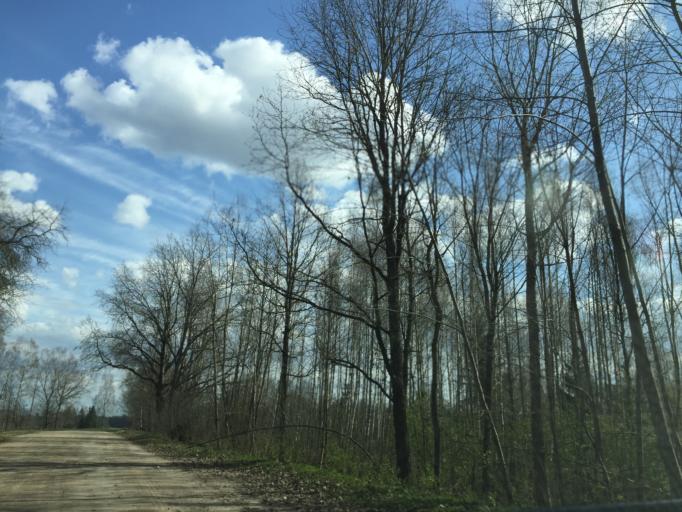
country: LV
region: Skriveri
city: Skriveri
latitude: 56.7990
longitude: 25.1398
